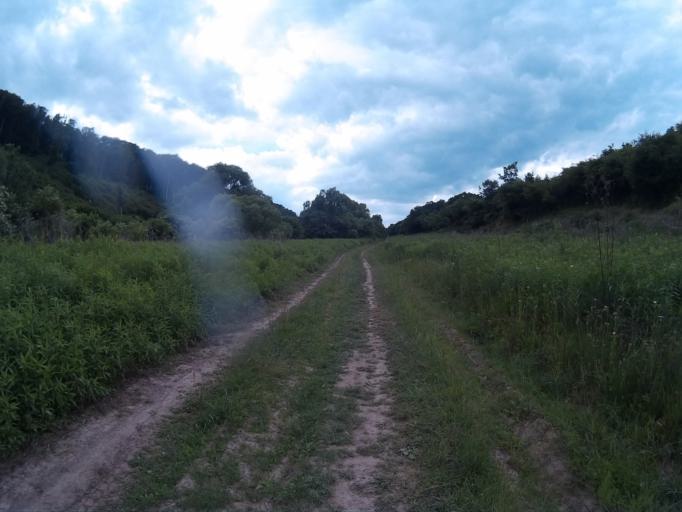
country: HU
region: Veszprem
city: Herend
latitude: 47.1049
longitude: 17.7626
